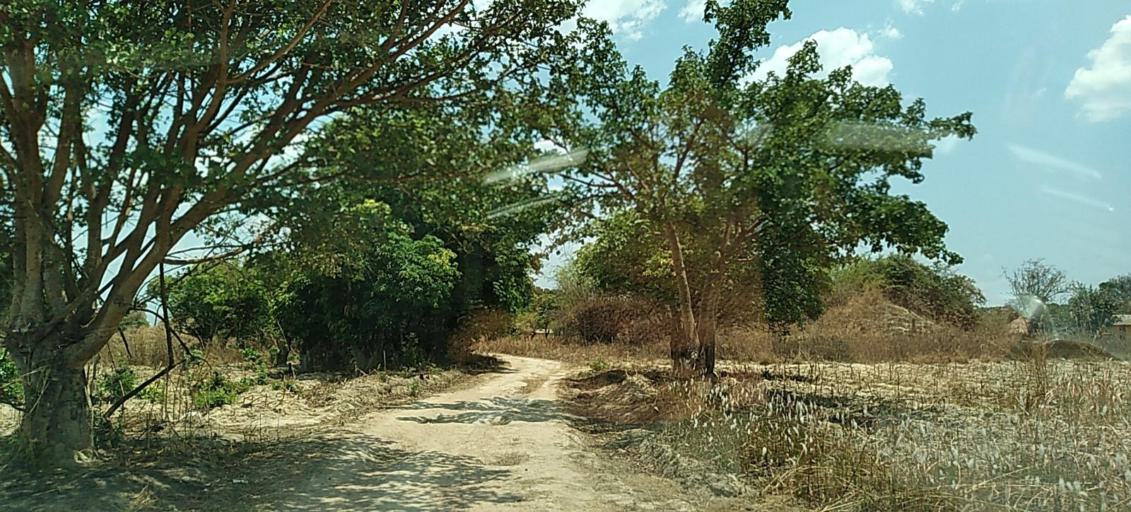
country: ZM
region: Copperbelt
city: Chililabombwe
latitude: -12.4741
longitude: 27.6655
